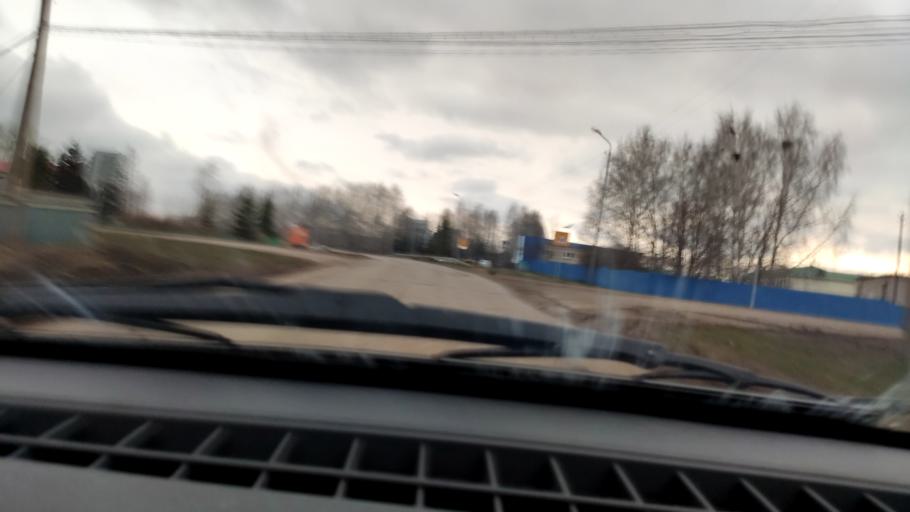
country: RU
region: Bashkortostan
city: Chekmagush
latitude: 55.1177
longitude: 54.4281
